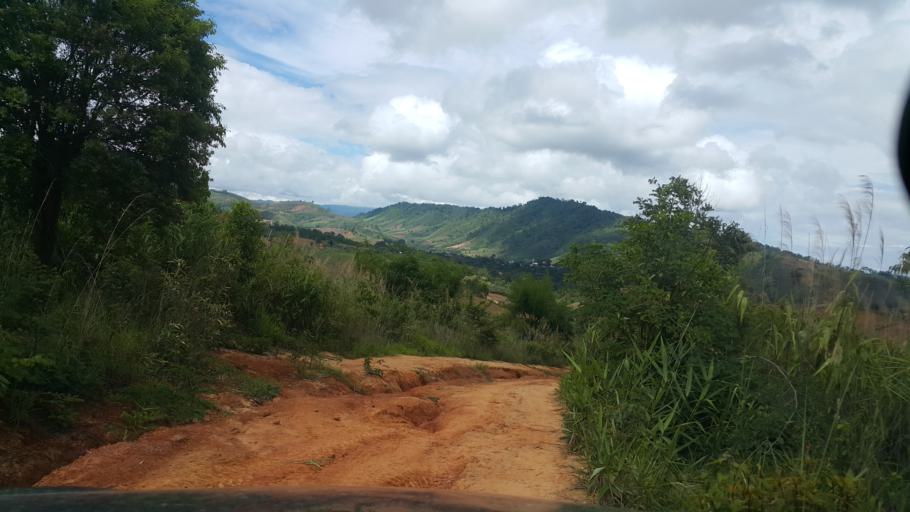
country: TH
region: Loei
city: Na Haeo
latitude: 17.5907
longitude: 100.8925
